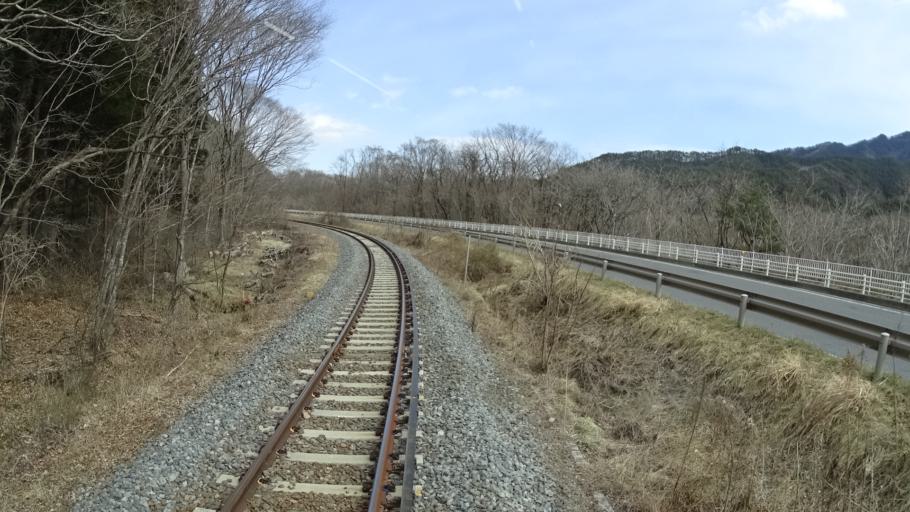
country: JP
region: Iwate
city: Yamada
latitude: 39.5473
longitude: 141.9390
